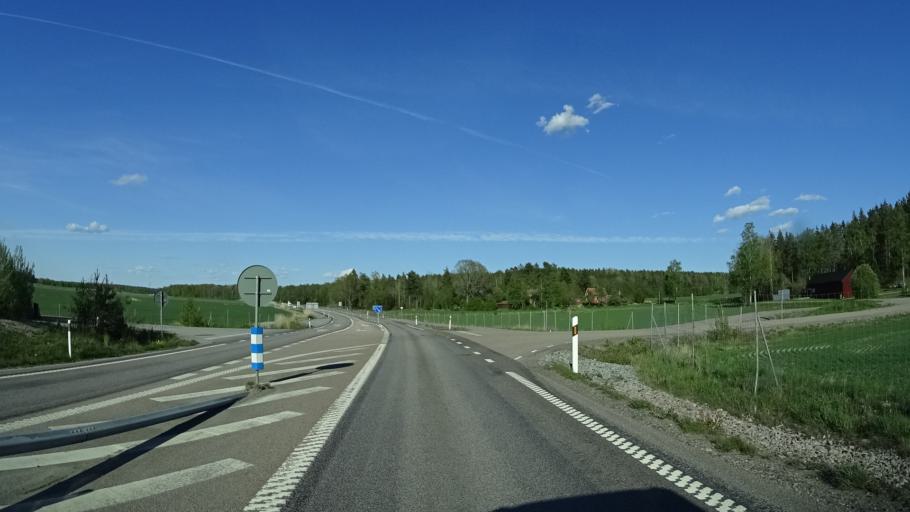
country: SE
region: Vaestmanland
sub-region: Kungsors Kommun
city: Kungsoer
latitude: 59.4094
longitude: 16.0321
